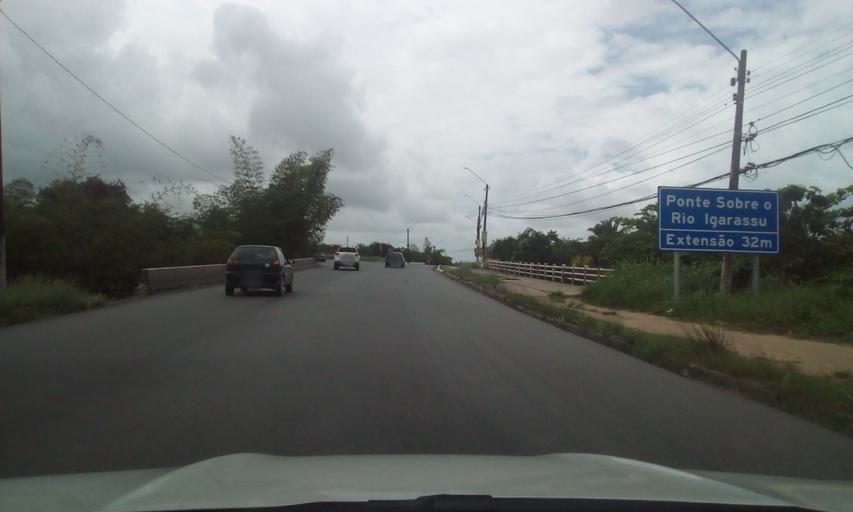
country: BR
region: Pernambuco
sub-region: Igarassu
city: Igarassu
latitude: -7.8355
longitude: -34.9125
